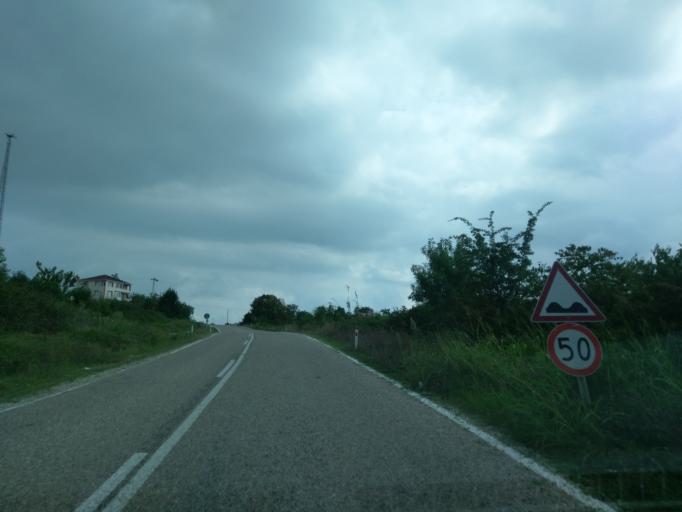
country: TR
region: Sinop
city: Erfelek
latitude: 41.9769
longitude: 34.8718
